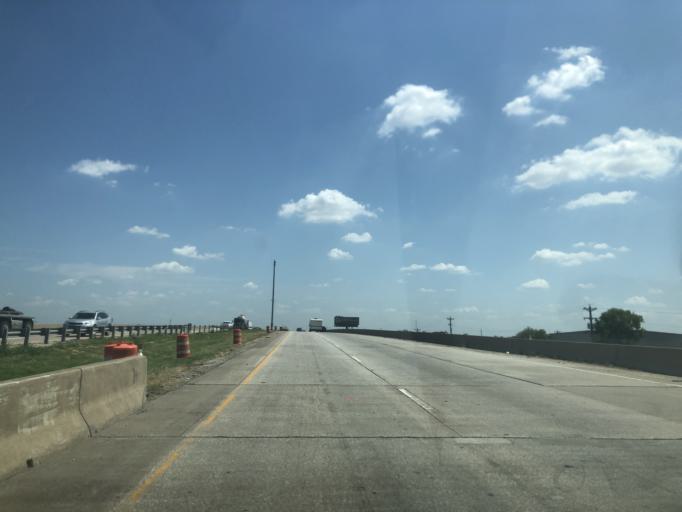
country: US
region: Texas
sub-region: Denton County
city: Sanger
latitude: 33.3170
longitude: -97.1800
